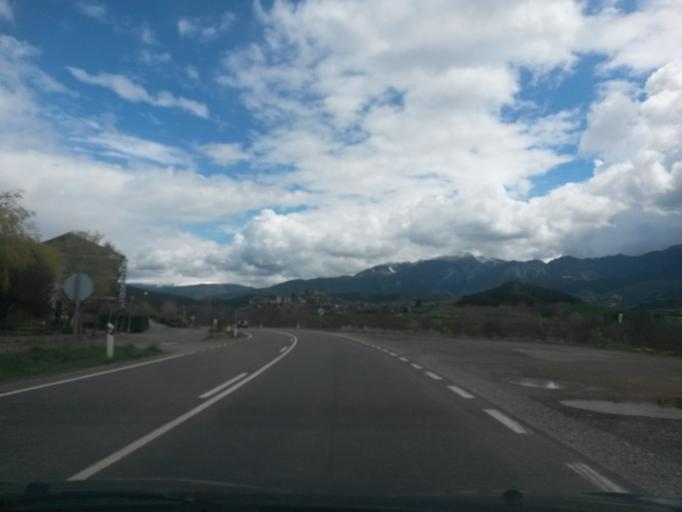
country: ES
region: Catalonia
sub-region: Provincia de Lleida
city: Bellver de Cerdanya
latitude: 42.3729
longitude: 1.7609
